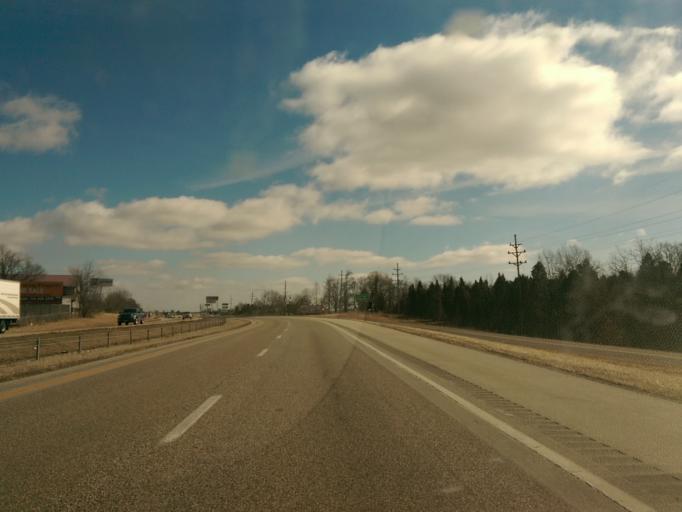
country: US
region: Missouri
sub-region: Montgomery County
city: Montgomery City
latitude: 38.8789
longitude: -91.3883
